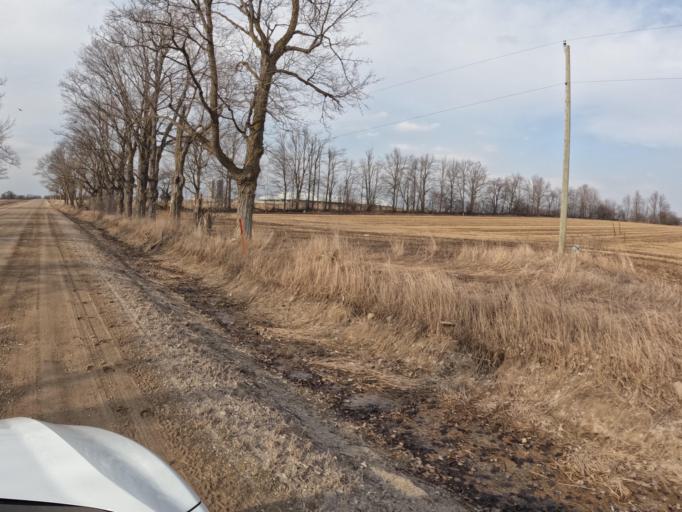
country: CA
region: Ontario
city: Orangeville
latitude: 43.8996
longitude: -80.2677
